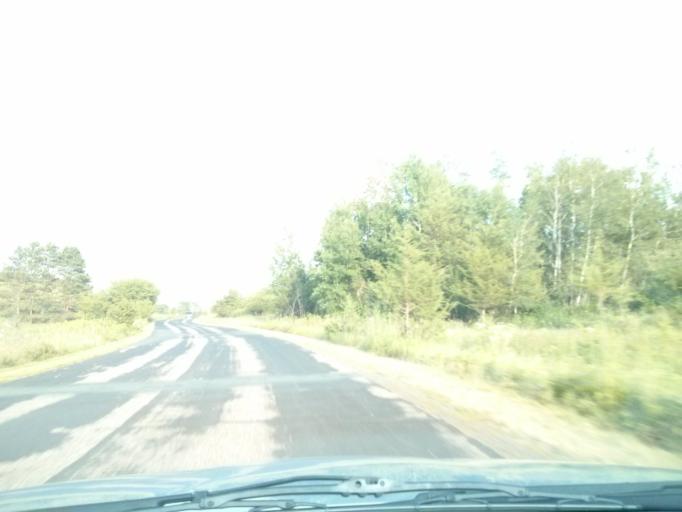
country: US
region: Wisconsin
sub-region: Saint Croix County
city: North Hudson
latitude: 45.0114
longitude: -92.6897
